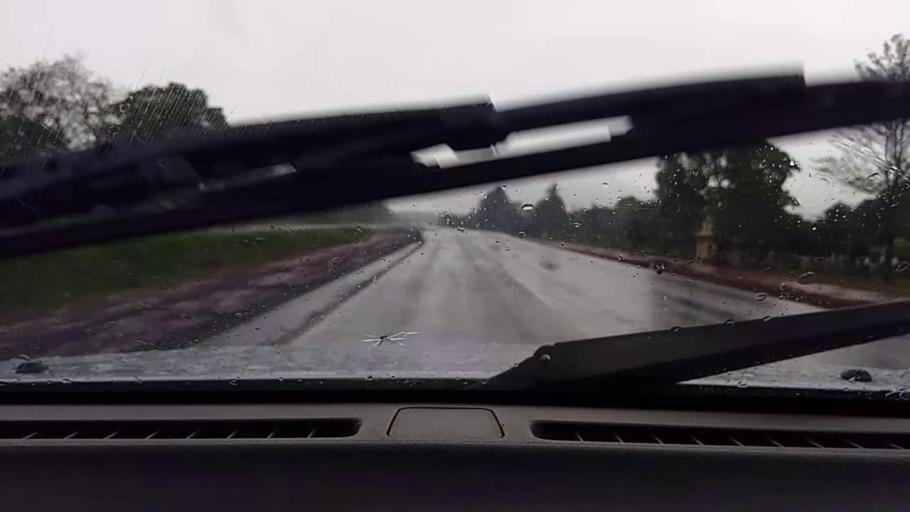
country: PY
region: Caaguazu
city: Repatriacion
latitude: -25.4599
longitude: -55.9225
